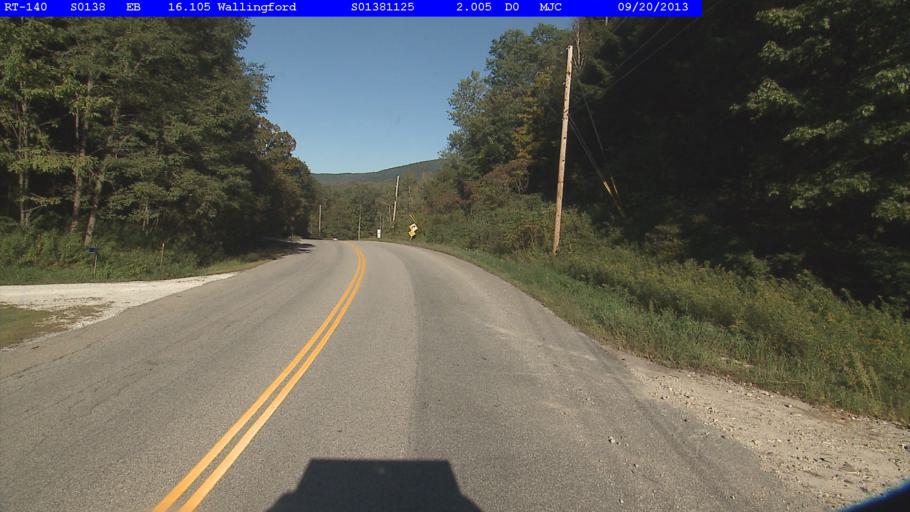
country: US
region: Vermont
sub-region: Rutland County
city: West Rutland
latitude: 43.4709
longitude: -72.9845
